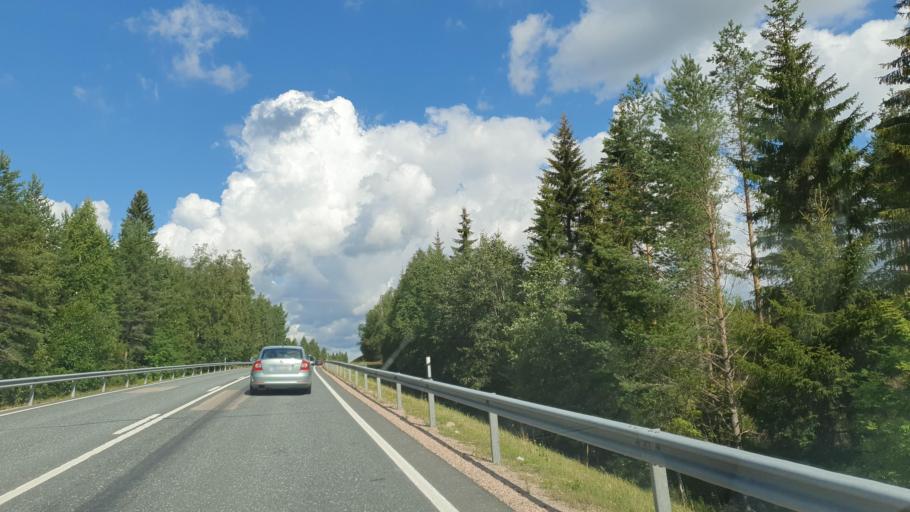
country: FI
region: Kainuu
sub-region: Kajaani
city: Kajaani
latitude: 64.0507
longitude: 27.4521
